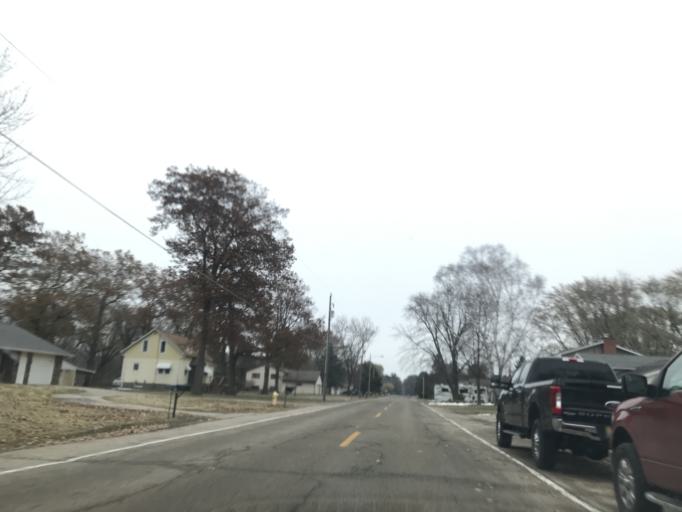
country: US
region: Wisconsin
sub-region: Marinette County
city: Marinette
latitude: 45.0781
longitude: -87.6221
